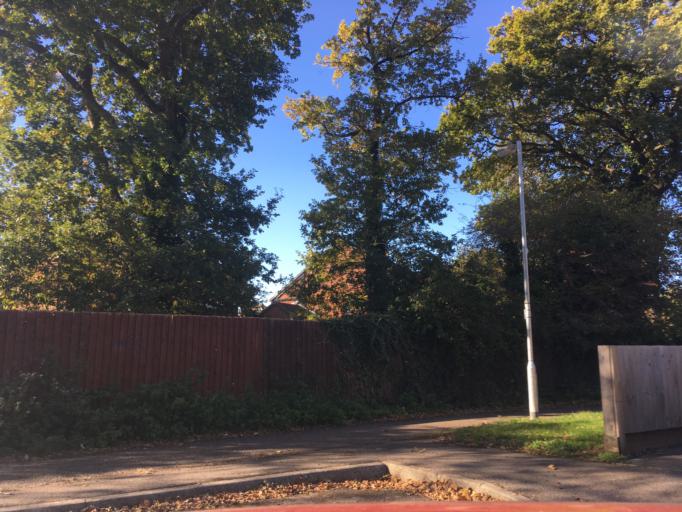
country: GB
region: England
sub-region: South Gloucestershire
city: Yate
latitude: 51.5504
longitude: -2.4208
